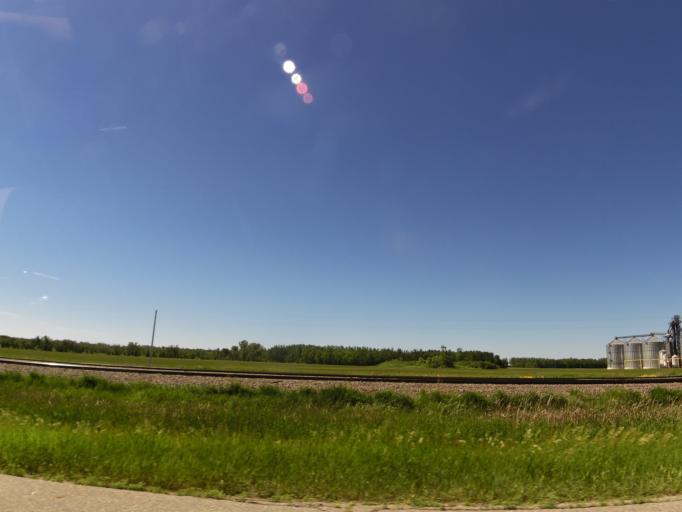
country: US
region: Minnesota
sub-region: Red Lake County
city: Red Lake Falls
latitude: 47.6874
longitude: -96.0670
